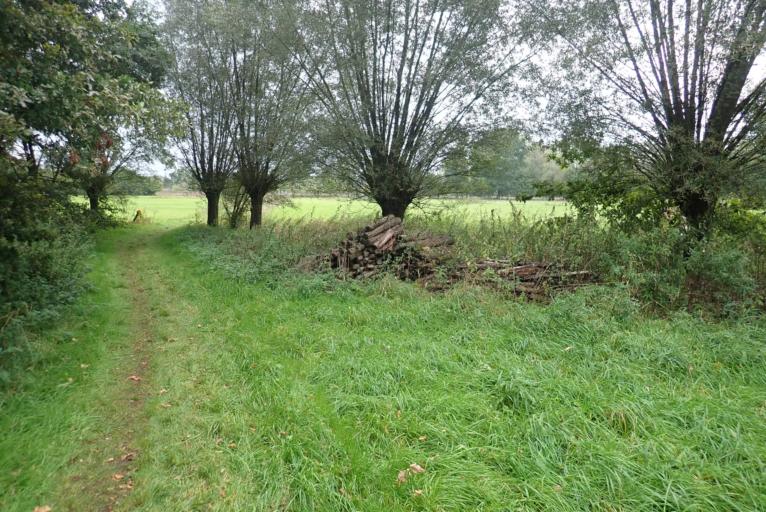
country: BE
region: Flanders
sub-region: Provincie Antwerpen
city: Hulshout
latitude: 51.0637
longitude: 4.7723
